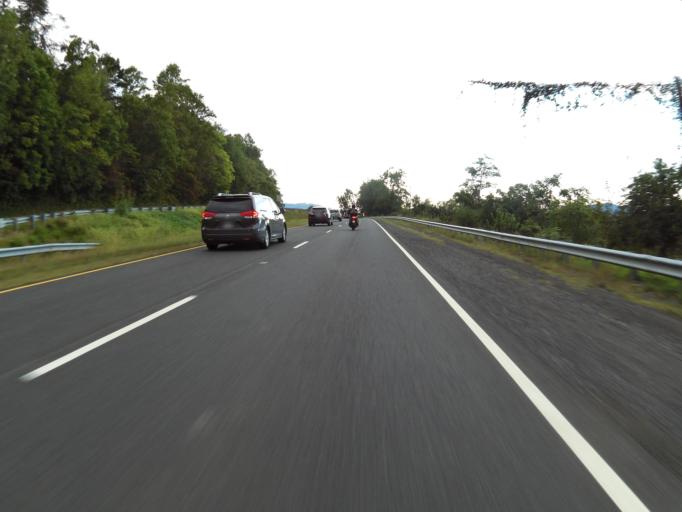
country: US
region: Virginia
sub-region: Rappahannock County
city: Washington
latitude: 38.6951
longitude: -78.1679
